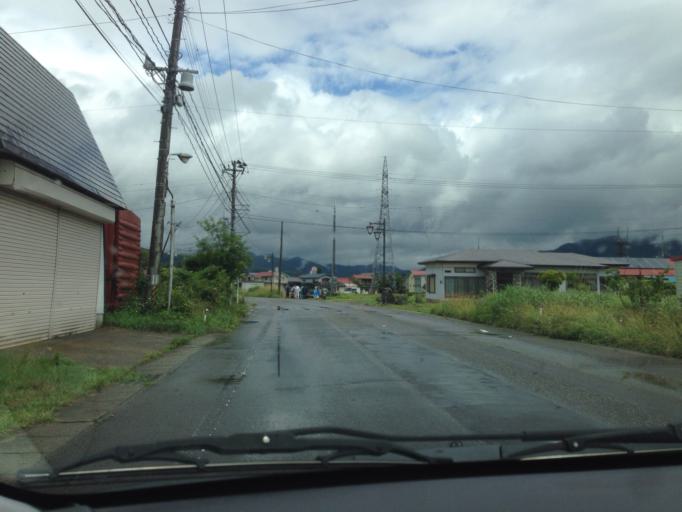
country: JP
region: Fukushima
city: Inawashiro
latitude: 37.5511
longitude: 140.1038
